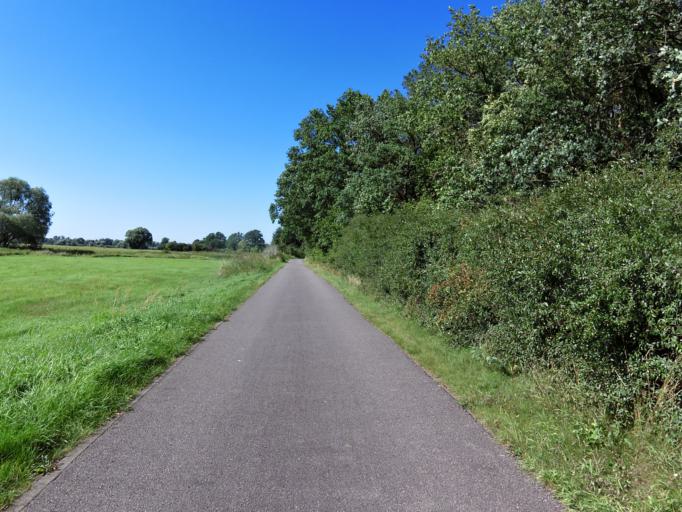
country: DE
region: Saxony-Anhalt
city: Muhlanger
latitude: 51.8559
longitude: 12.7173
